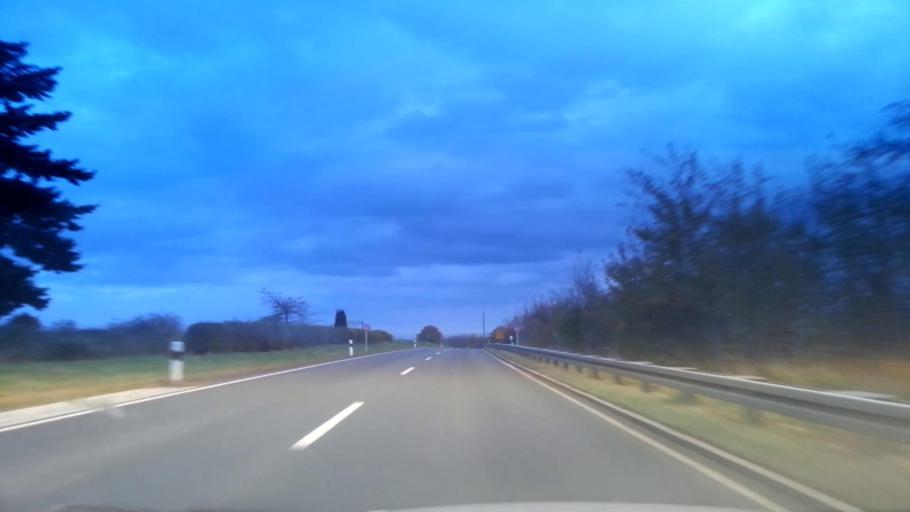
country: DE
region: Bavaria
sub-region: Upper Palatinate
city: Mitterteich
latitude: 49.9513
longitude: 12.2074
